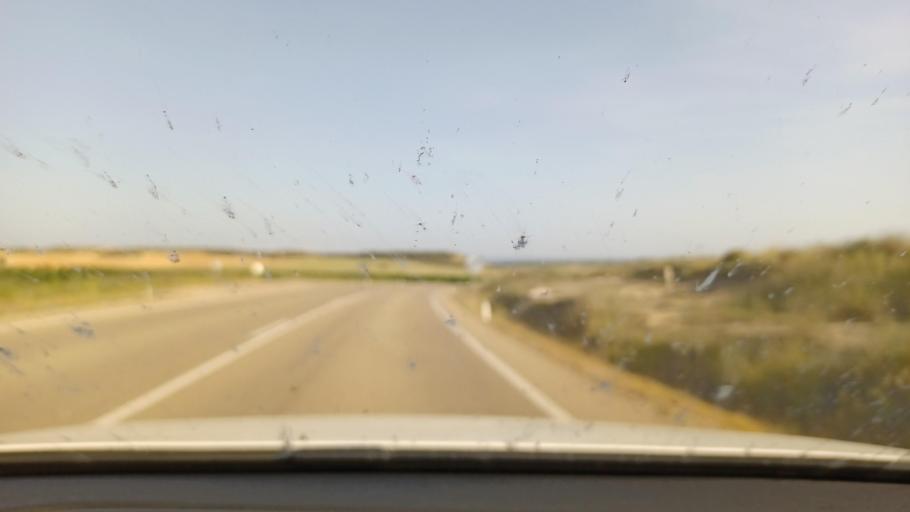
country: ES
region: Aragon
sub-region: Provincia de Zaragoza
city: Chiprana
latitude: 41.3044
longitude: -0.0702
